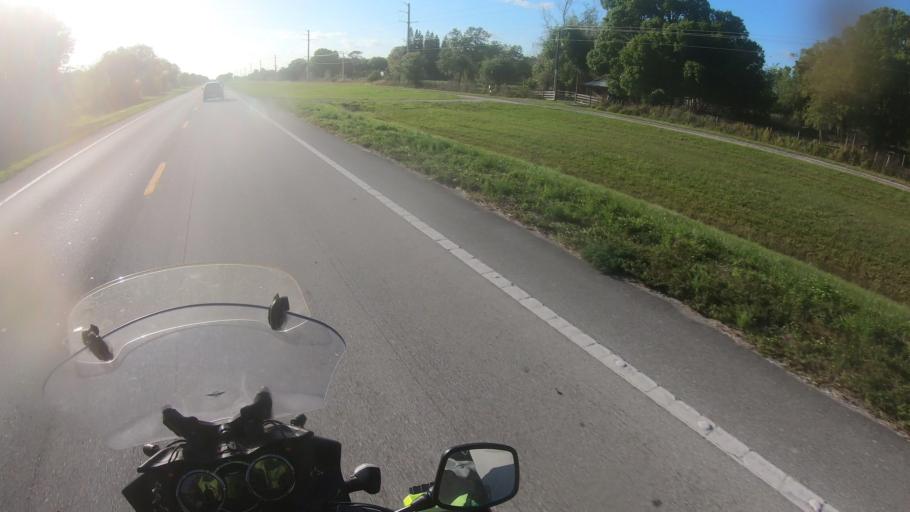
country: US
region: Florida
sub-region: DeSoto County
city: Southeast Arcadia
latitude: 27.2091
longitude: -81.7648
